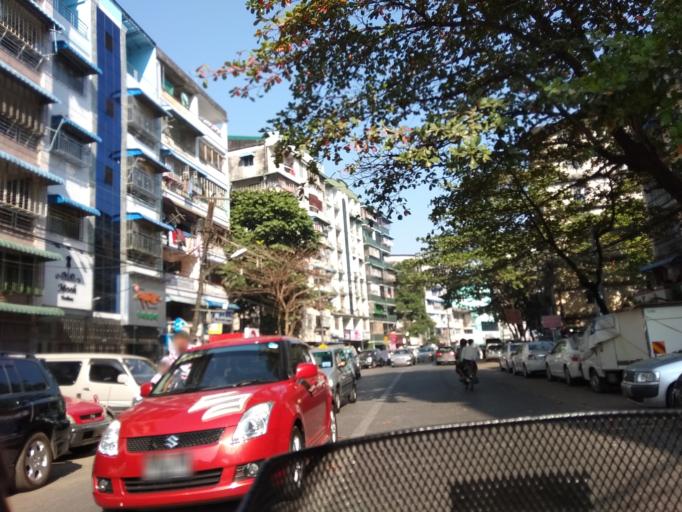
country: MM
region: Yangon
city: Yangon
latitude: 16.8048
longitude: 96.1330
